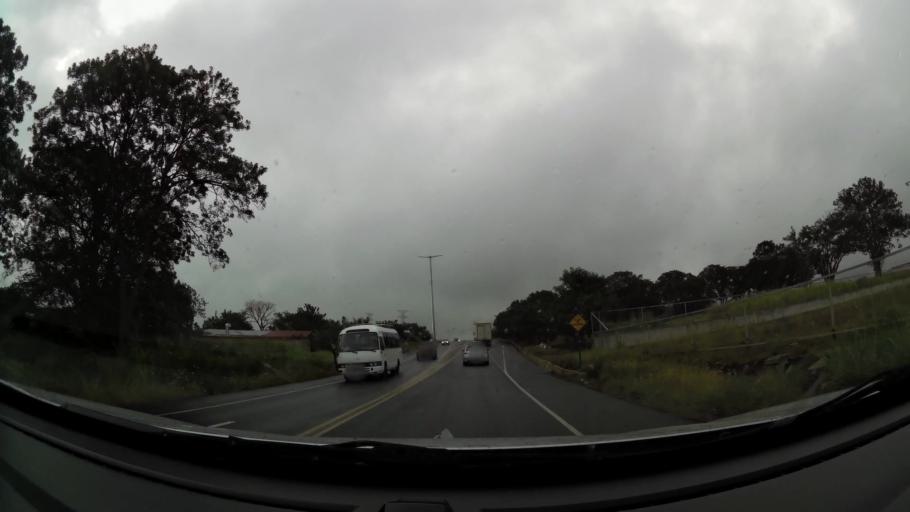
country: CR
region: Alajuela
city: Carrillos
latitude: 9.9885
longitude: -84.2693
